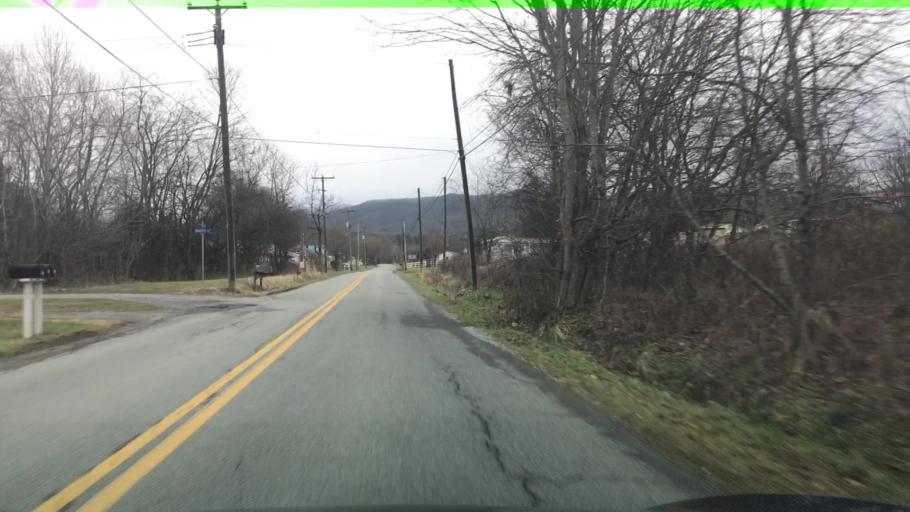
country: US
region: Virginia
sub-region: Smyth County
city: Atkins
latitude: 36.7722
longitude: -81.4077
